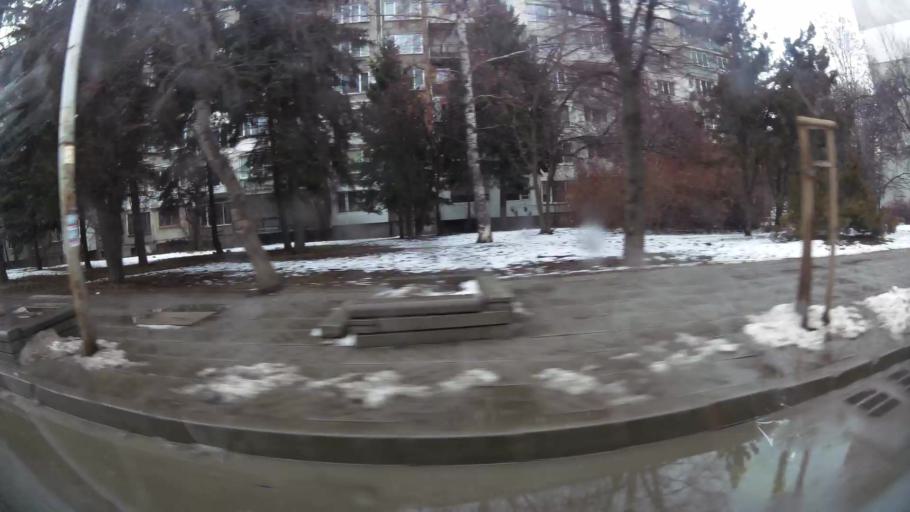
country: BG
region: Sofia-Capital
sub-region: Stolichna Obshtina
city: Sofia
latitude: 42.6630
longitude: 23.2927
